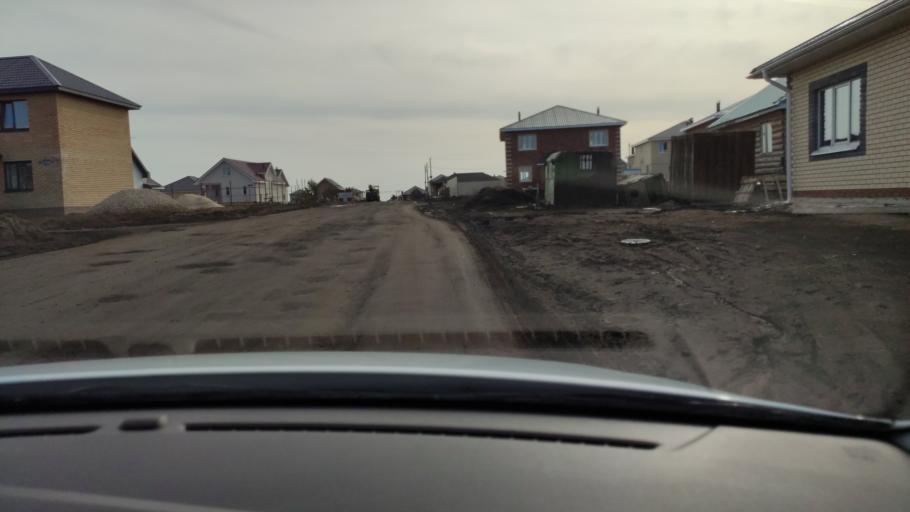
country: RU
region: Tatarstan
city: Stolbishchi
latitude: 55.7184
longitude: 49.3324
